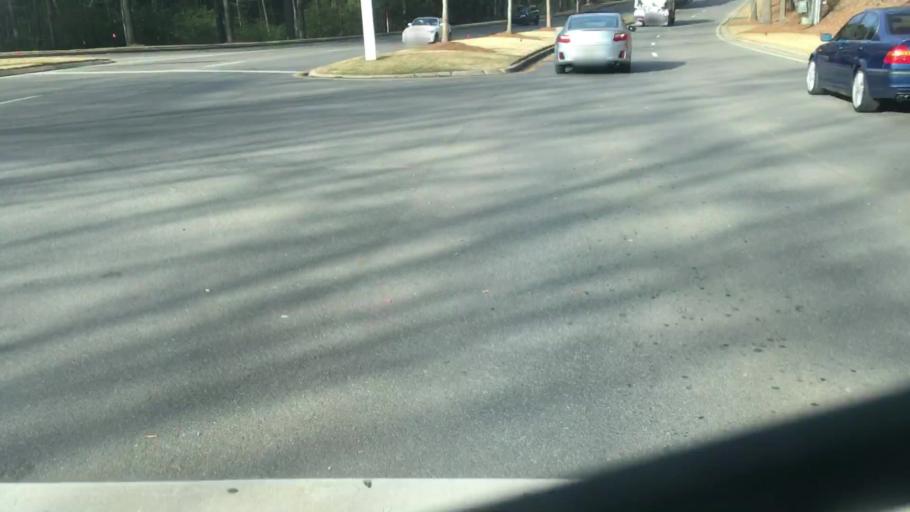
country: US
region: Alabama
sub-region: Jefferson County
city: Cahaba Heights
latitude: 33.4865
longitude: -86.7083
